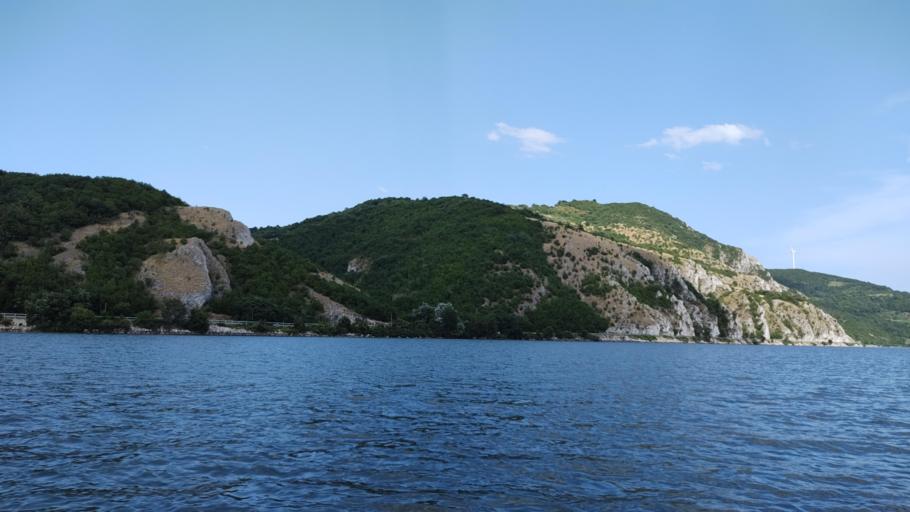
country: RO
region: Caras-Severin
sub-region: Comuna Pescari
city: Coronini
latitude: 44.6673
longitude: 21.6870
